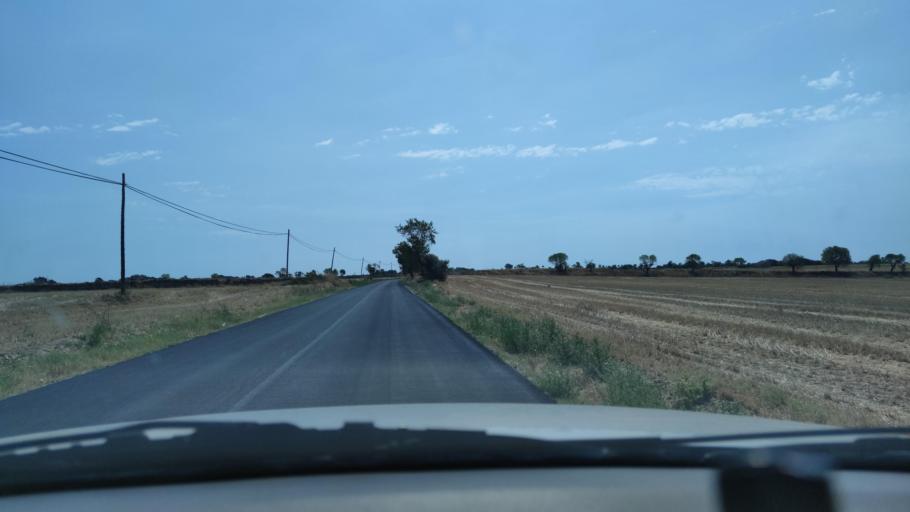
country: ES
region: Catalonia
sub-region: Provincia de Lleida
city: Ivorra
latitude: 41.7801
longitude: 1.3085
